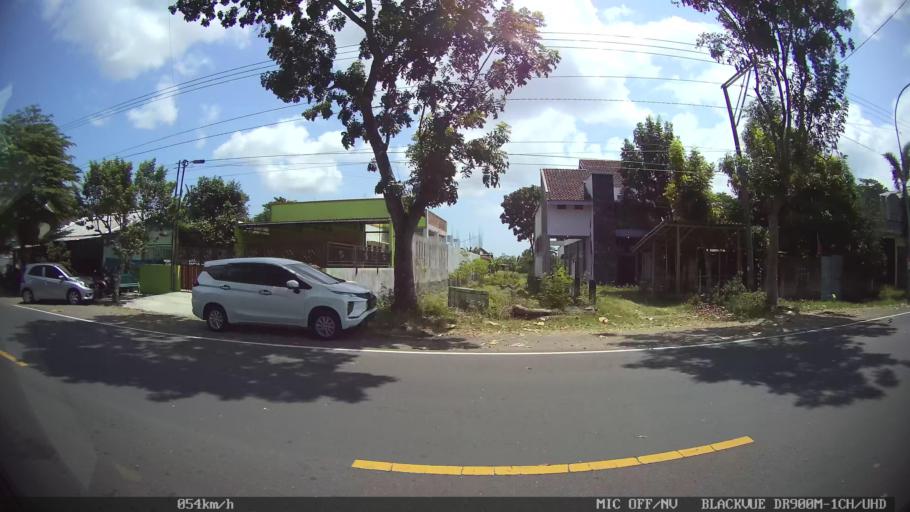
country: ID
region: Daerah Istimewa Yogyakarta
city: Bantul
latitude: -7.8941
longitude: 110.3468
